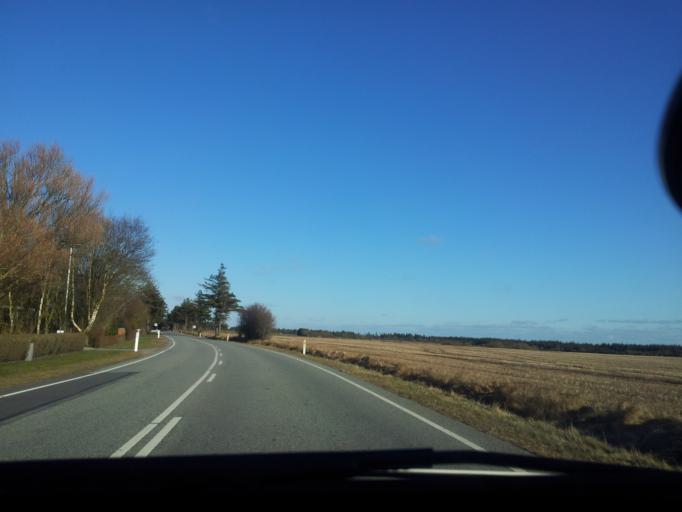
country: DE
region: Schleswig-Holstein
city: Klanxbull
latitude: 55.0194
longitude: 8.6597
